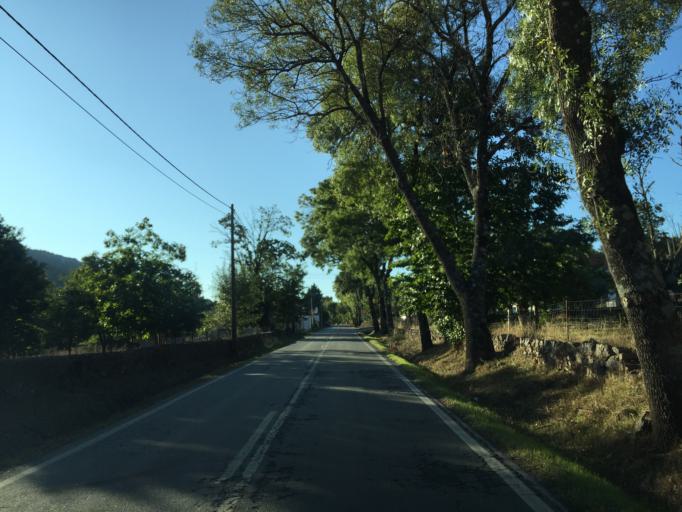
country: PT
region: Portalegre
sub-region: Marvao
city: Marvao
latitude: 39.3936
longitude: -7.4171
